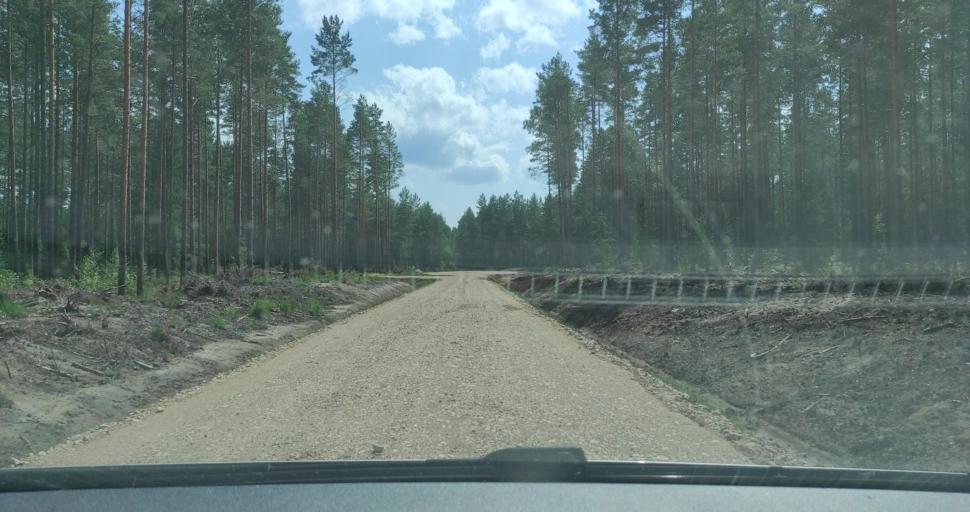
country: LV
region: Kuldigas Rajons
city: Kuldiga
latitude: 57.0540
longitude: 22.1905
